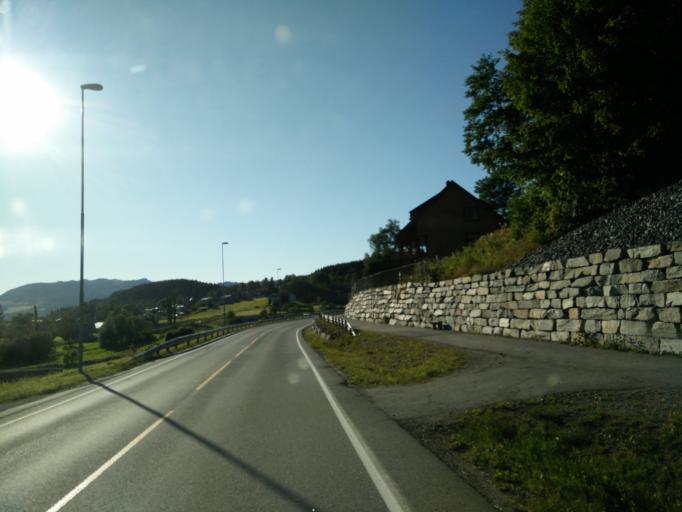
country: NO
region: More og Romsdal
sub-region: Halsa
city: Liaboen
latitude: 63.0873
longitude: 8.3582
